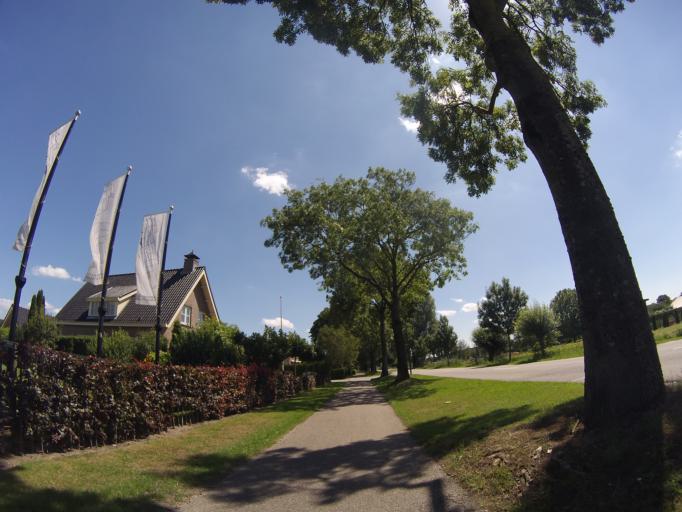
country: NL
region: Utrecht
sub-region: Stichtse Vecht
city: Maarssen
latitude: 52.1389
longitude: 5.0799
